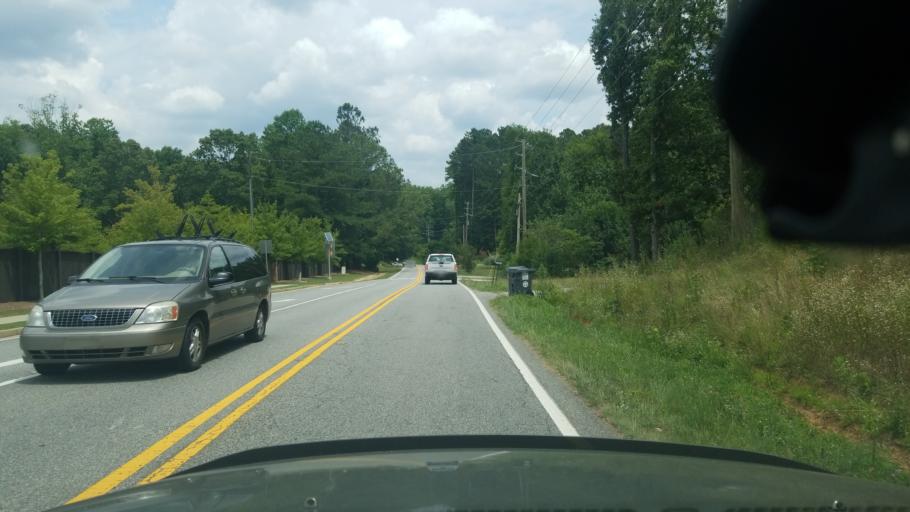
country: US
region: Georgia
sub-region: Forsyth County
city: Cumming
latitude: 34.2125
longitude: -84.2111
